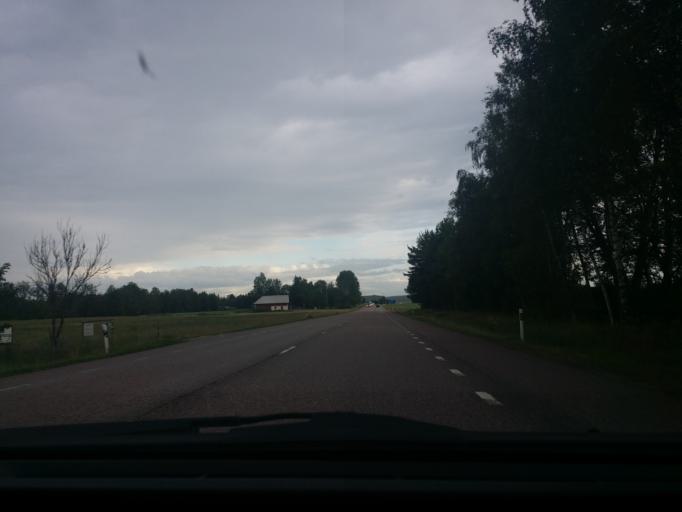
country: SE
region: OErebro
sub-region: Orebro Kommun
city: Hovsta
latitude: 59.4291
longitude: 15.1702
